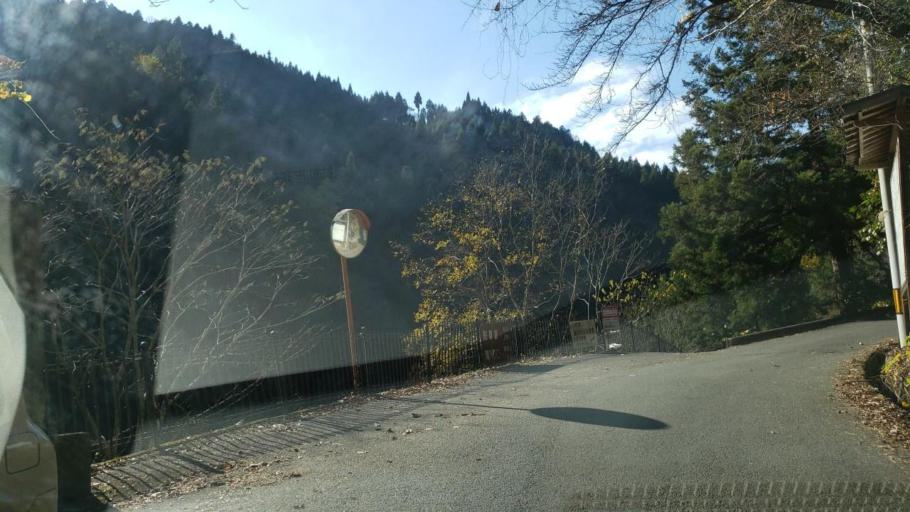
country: JP
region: Tokushima
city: Wakimachi
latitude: 33.9906
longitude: 134.0018
